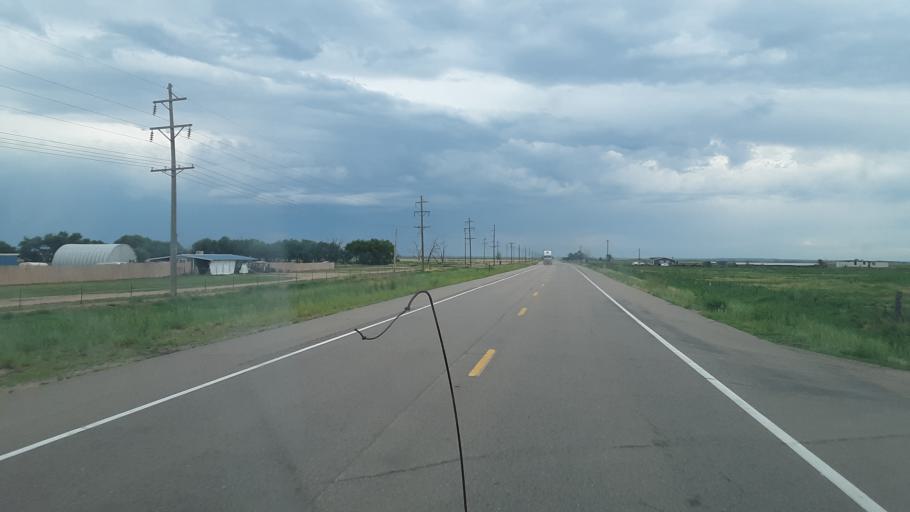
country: US
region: Colorado
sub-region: Crowley County
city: Ordway
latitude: 38.2016
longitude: -103.7482
